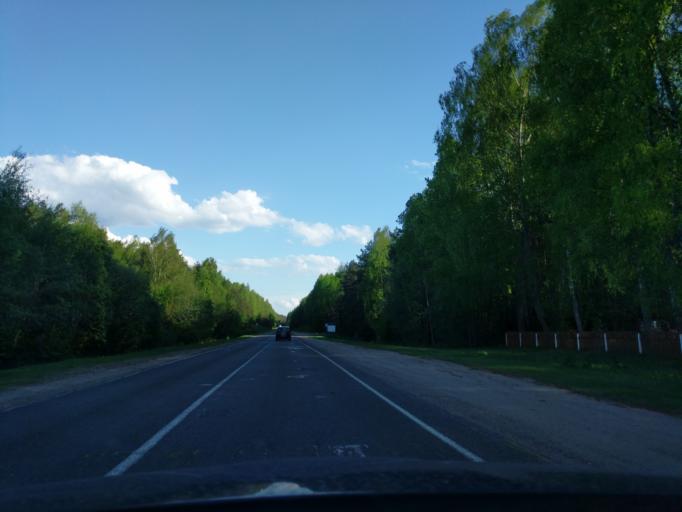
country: BY
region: Minsk
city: Kryvichy
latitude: 54.6053
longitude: 27.1827
